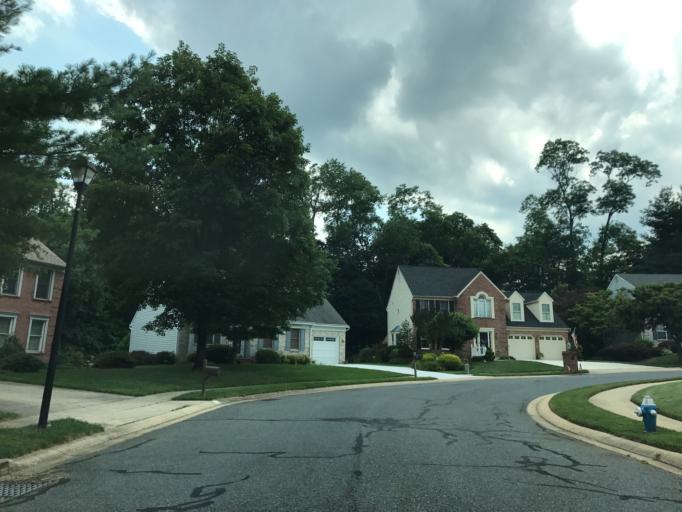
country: US
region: Maryland
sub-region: Harford County
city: North Bel Air
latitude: 39.5405
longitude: -76.3608
